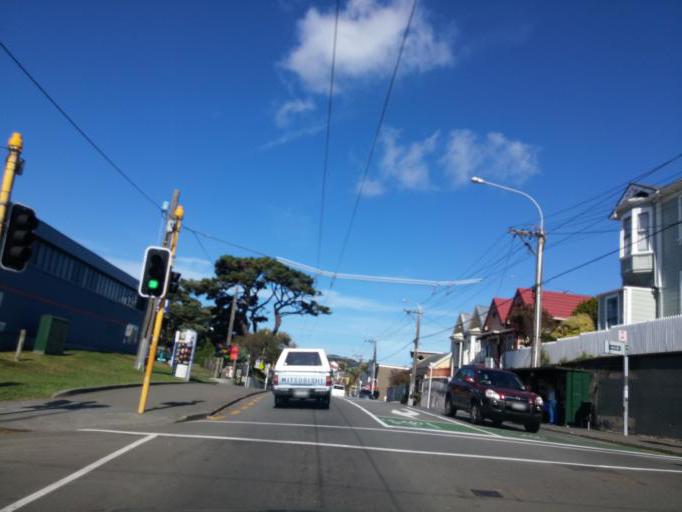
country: NZ
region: Wellington
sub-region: Wellington City
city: Wellington
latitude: -41.3017
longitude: 174.7740
